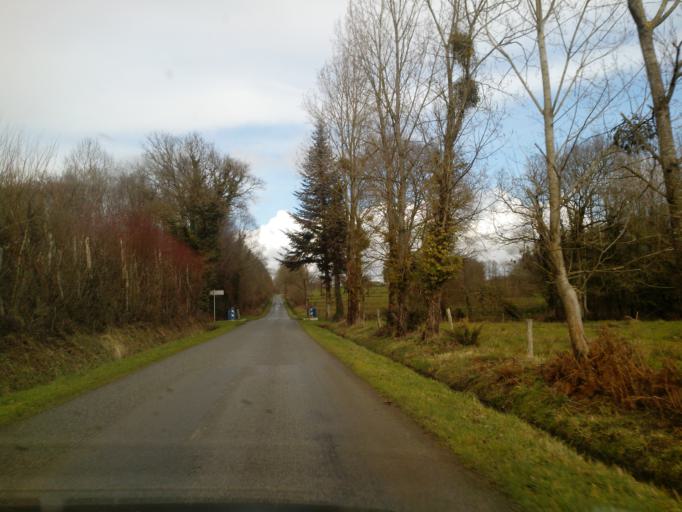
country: FR
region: Brittany
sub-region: Departement des Cotes-d'Armor
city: Merdrignac
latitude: 48.1722
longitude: -2.4192
